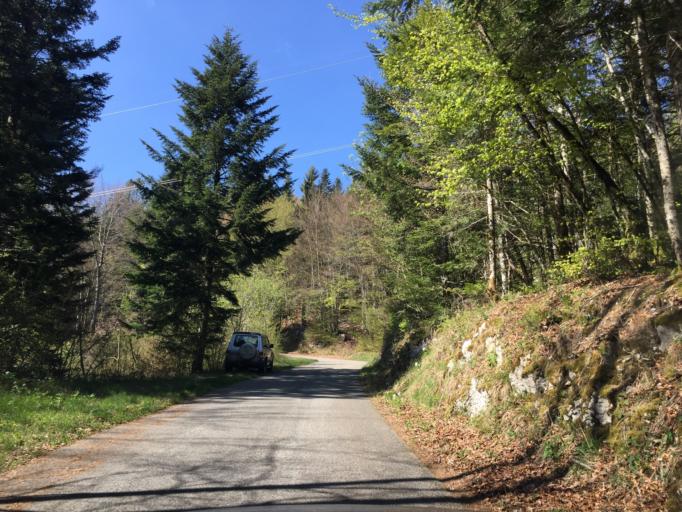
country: FR
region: Rhone-Alpes
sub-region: Departement de la Savoie
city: Novalaise
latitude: 45.5880
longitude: 5.8142
